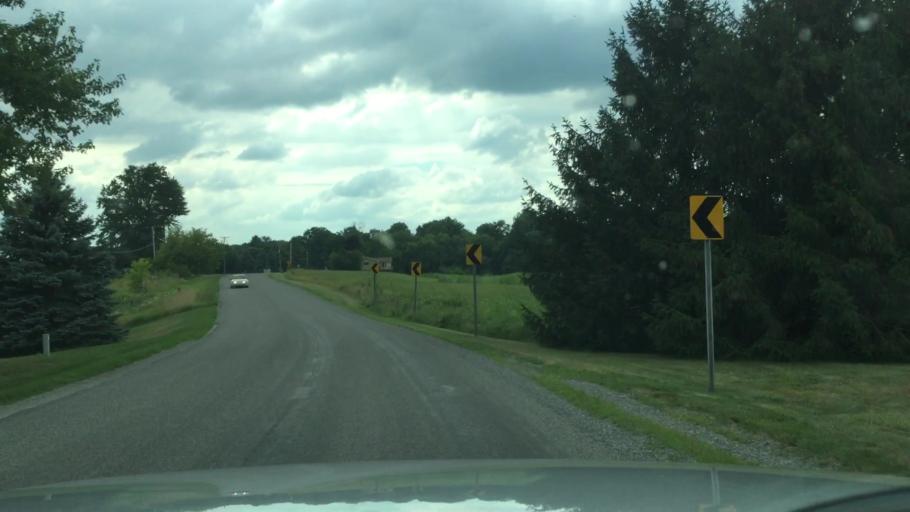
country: US
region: Michigan
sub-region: Saginaw County
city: Frankenmuth
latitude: 43.3217
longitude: -83.8002
